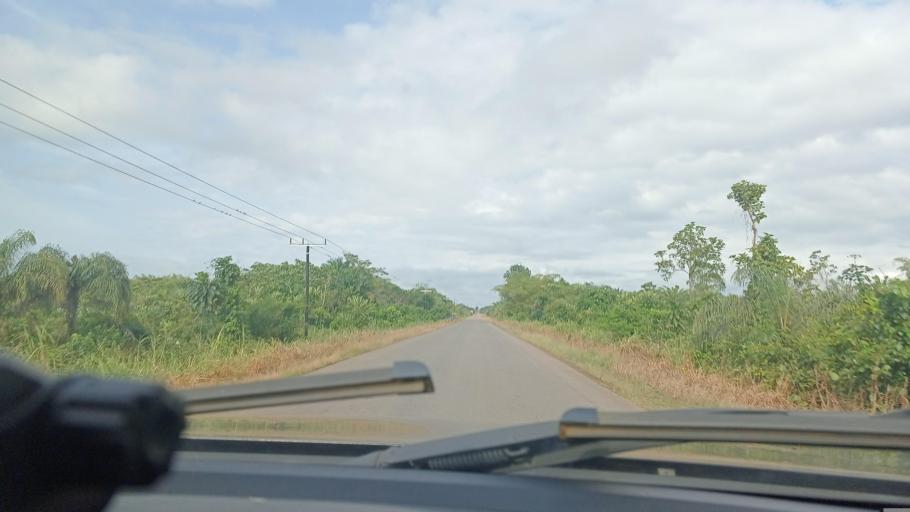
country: LR
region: Bomi
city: Tubmanburg
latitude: 6.7121
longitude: -10.9547
